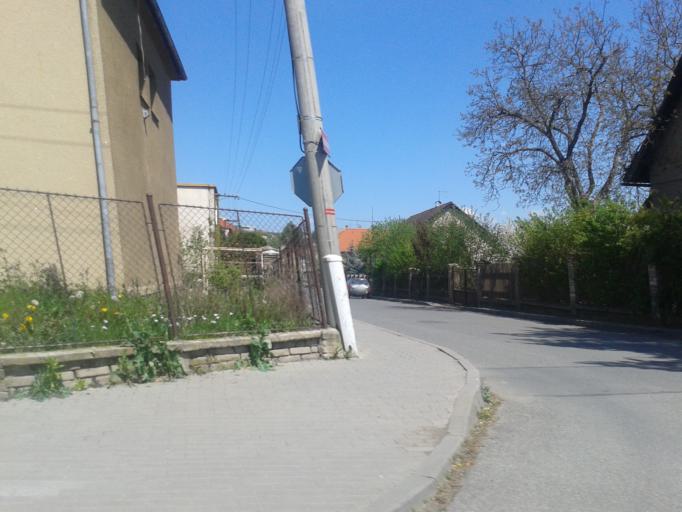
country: CZ
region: Central Bohemia
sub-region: Okres Beroun
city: Kraluv Dvur
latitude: 49.9479
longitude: 14.0319
